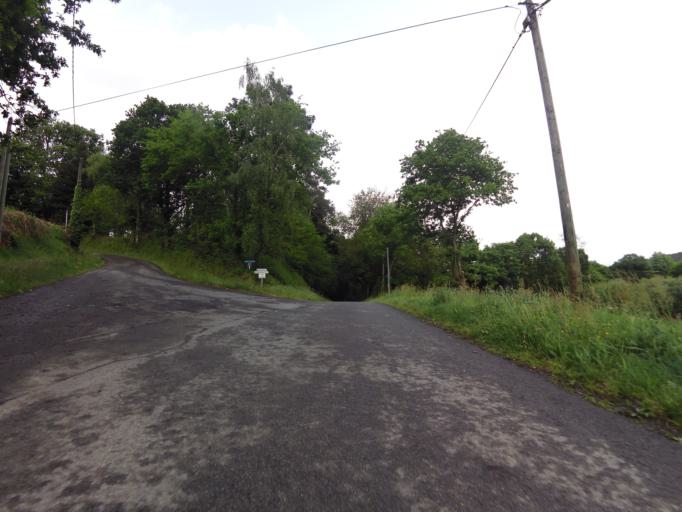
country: FR
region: Brittany
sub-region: Departement du Morbihan
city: Pluherlin
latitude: 47.7117
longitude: -2.3772
